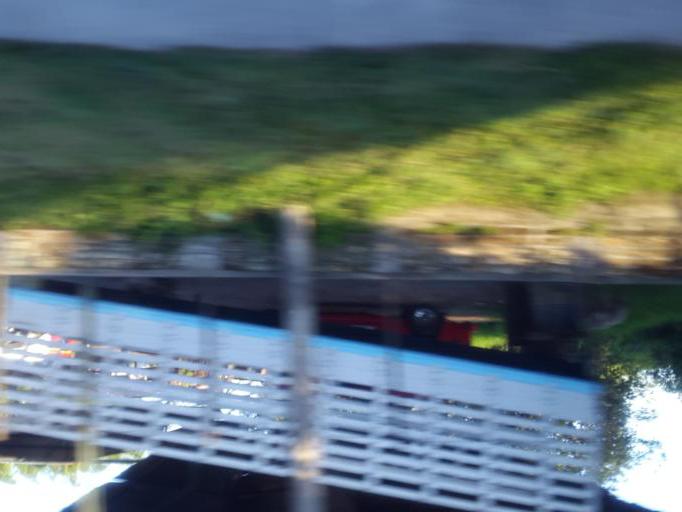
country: CO
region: Quindio
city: Montenegro
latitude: 4.5596
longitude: -75.7488
